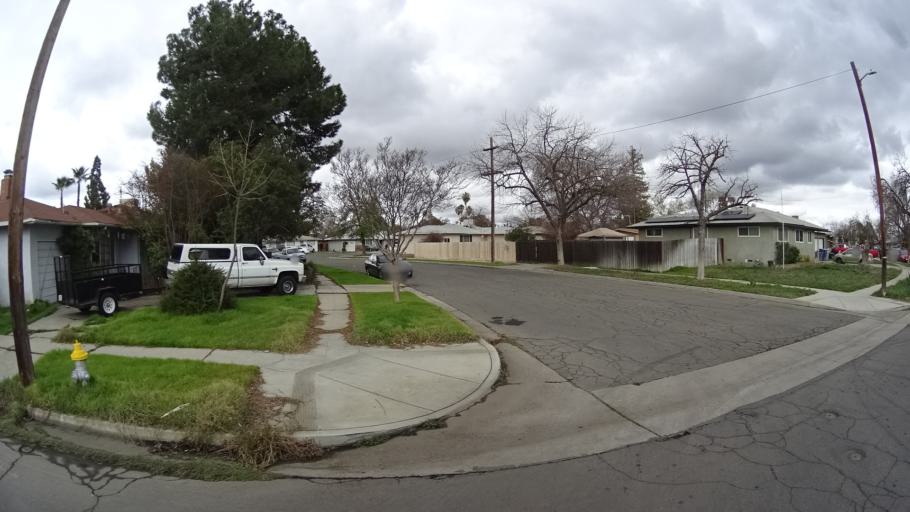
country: US
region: California
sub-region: Fresno County
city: Fresno
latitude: 36.7878
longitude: -119.8387
